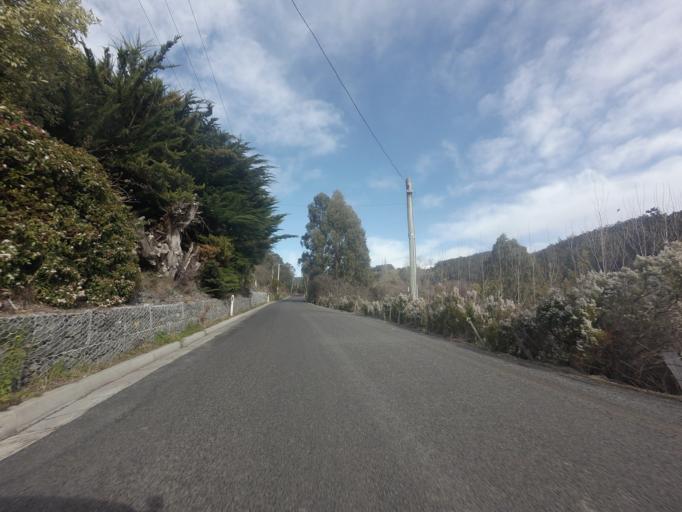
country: AU
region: Tasmania
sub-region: Kingborough
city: Margate
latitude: -42.9897
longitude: 147.1893
